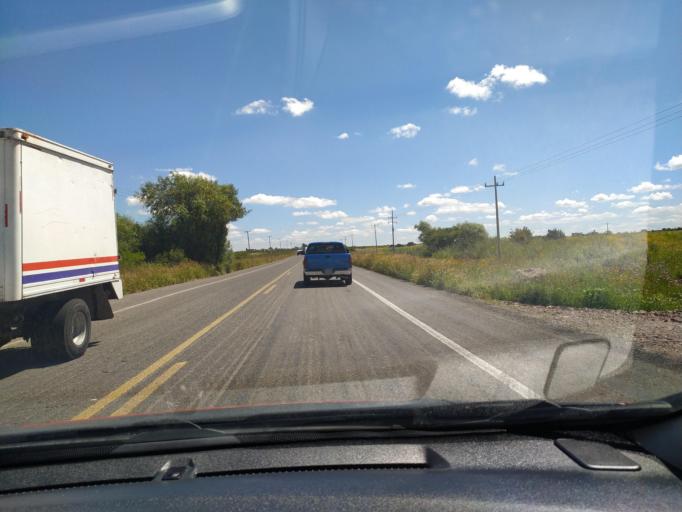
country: MX
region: Jalisco
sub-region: San Julian
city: Colonia Veintitres de Mayo
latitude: 21.0090
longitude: -102.2491
